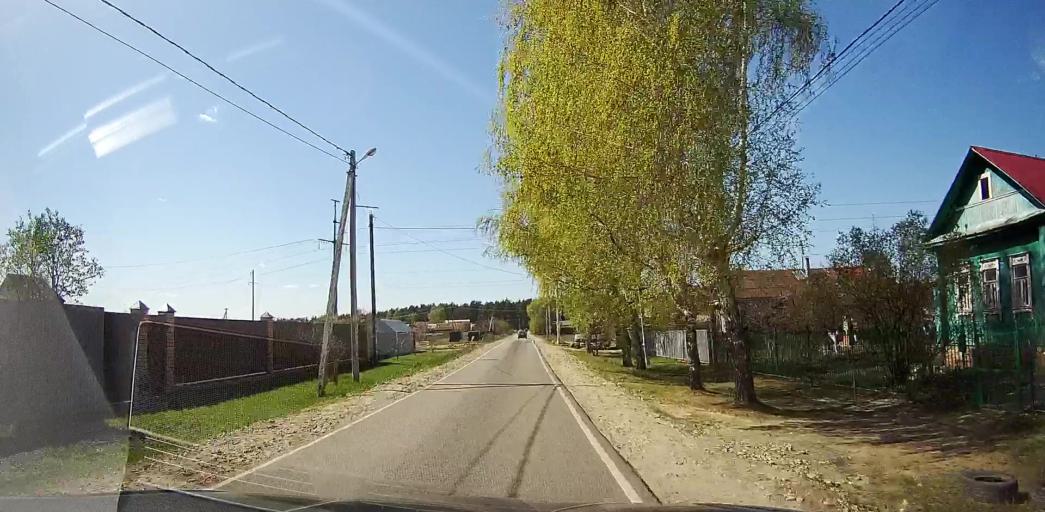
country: RU
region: Moskovskaya
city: Malyshevo
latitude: 55.4622
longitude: 38.3396
